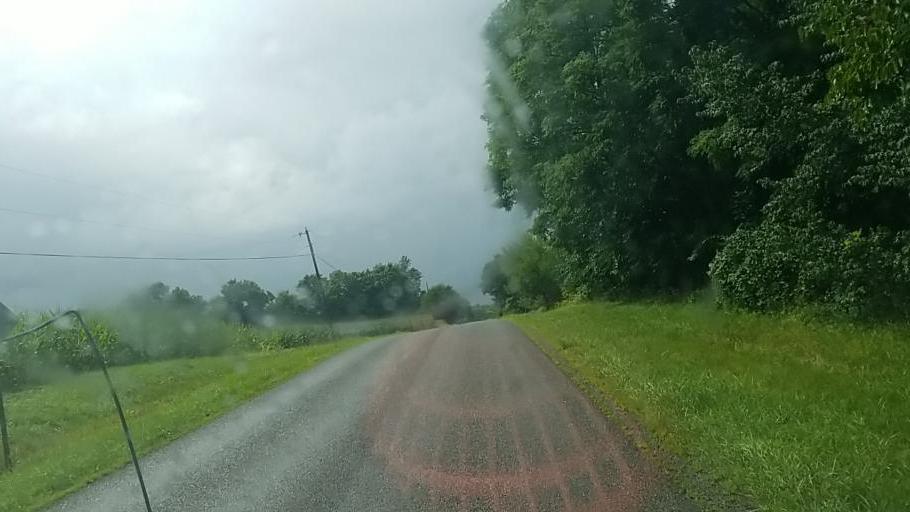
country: US
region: Ohio
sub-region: Champaign County
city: North Lewisburg
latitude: 40.3116
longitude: -83.6235
